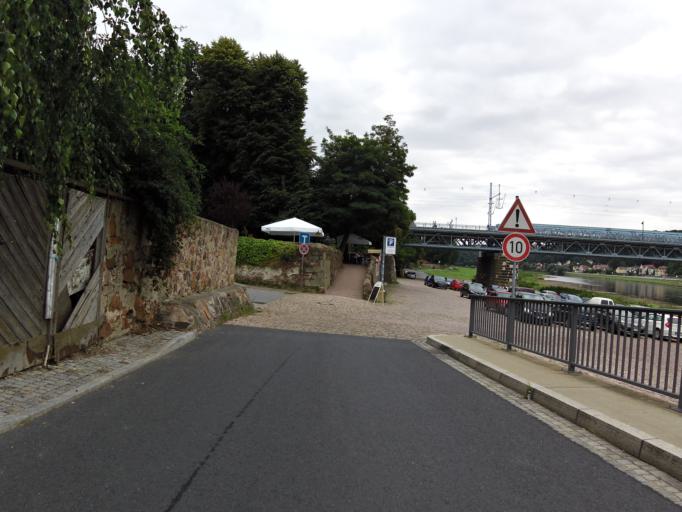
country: DE
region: Saxony
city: Meissen
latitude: 51.1632
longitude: 13.4796
